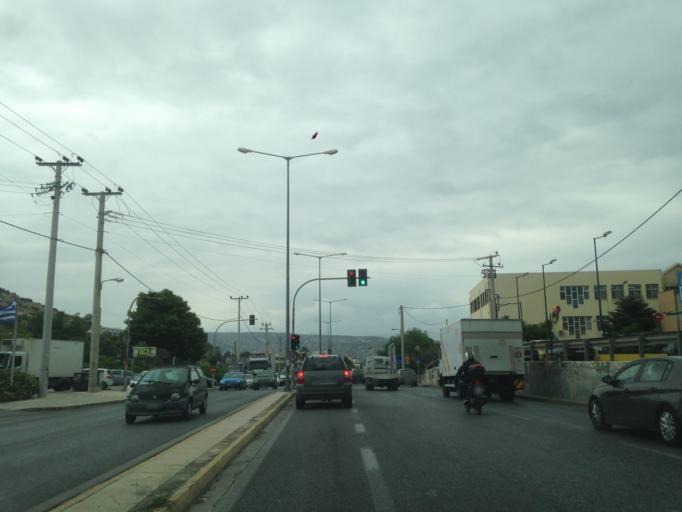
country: GR
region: Attica
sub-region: Nomarchia Anatolikis Attikis
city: Vari
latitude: 37.8347
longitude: 23.7943
